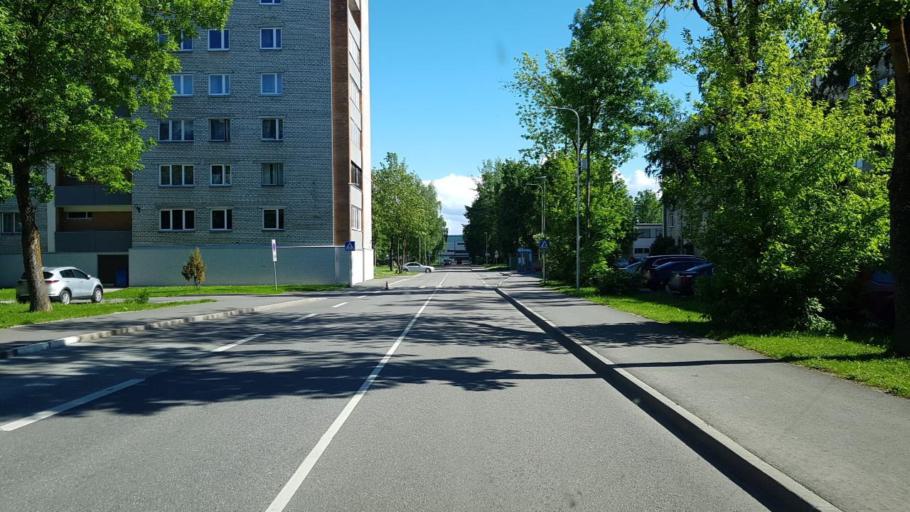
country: EE
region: Ida-Virumaa
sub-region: Narva linn
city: Narva
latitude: 59.3672
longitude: 28.1813
